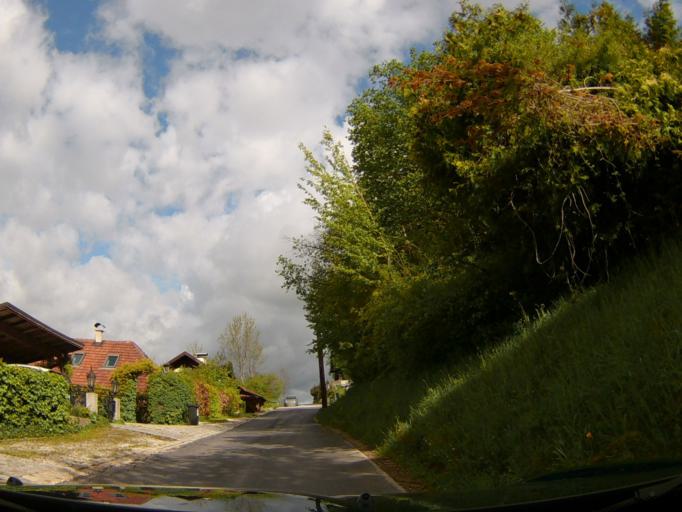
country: AT
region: Upper Austria
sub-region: Politischer Bezirk Vocklabruck
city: Mondsee
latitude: 47.8660
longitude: 13.3553
